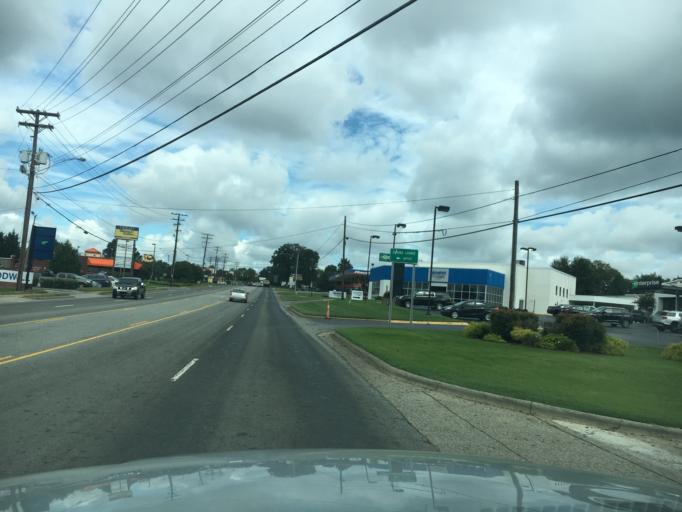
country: US
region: North Carolina
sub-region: Catawba County
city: Hickory
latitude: 35.7160
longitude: -81.3135
